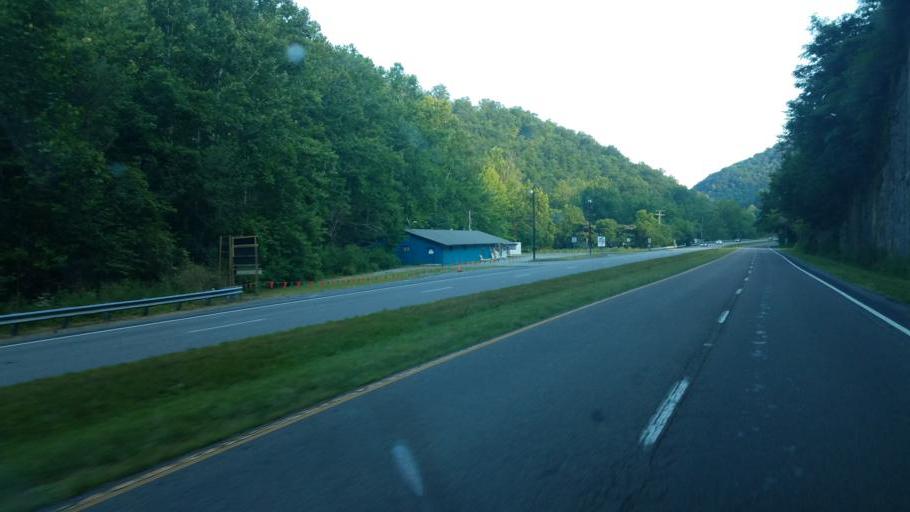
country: US
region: Tennessee
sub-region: Hawkins County
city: Church Hill
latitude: 36.6820
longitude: -82.7557
